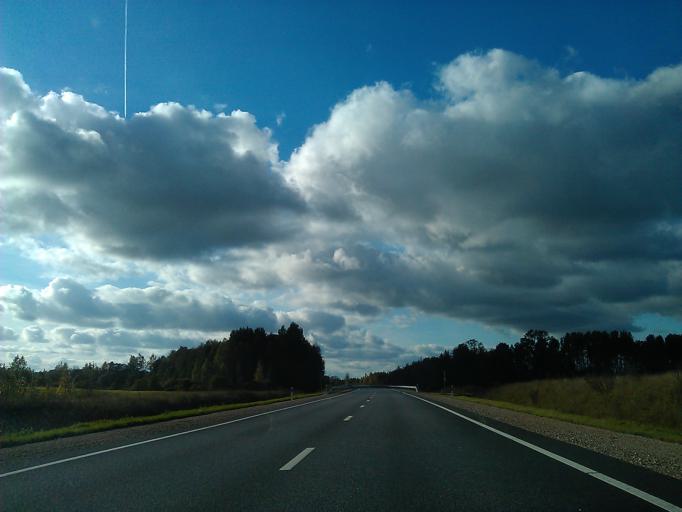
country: LV
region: Skriveri
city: Skriveri
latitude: 56.7724
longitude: 25.0776
